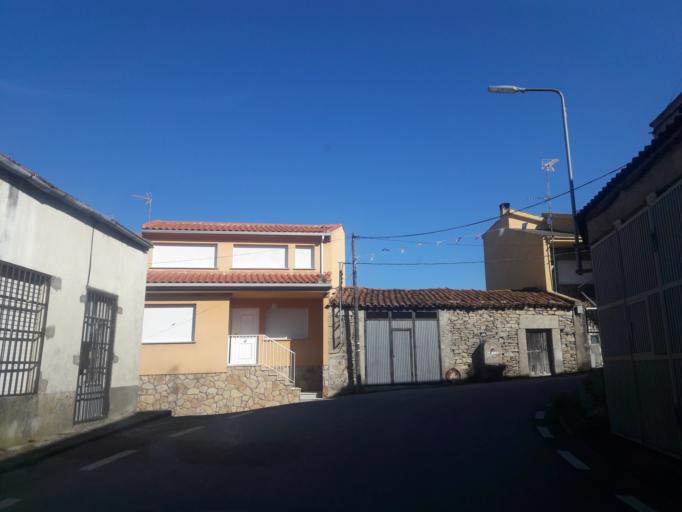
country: ES
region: Castille and Leon
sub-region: Provincia de Salamanca
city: Cabeza del Caballo
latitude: 41.1287
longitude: -6.5578
